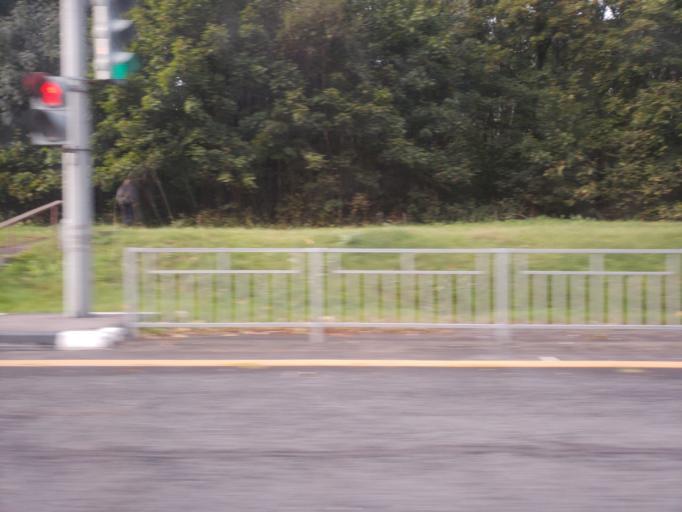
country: RU
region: Moskovskaya
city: Petrovskaya
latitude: 55.5453
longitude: 37.7971
